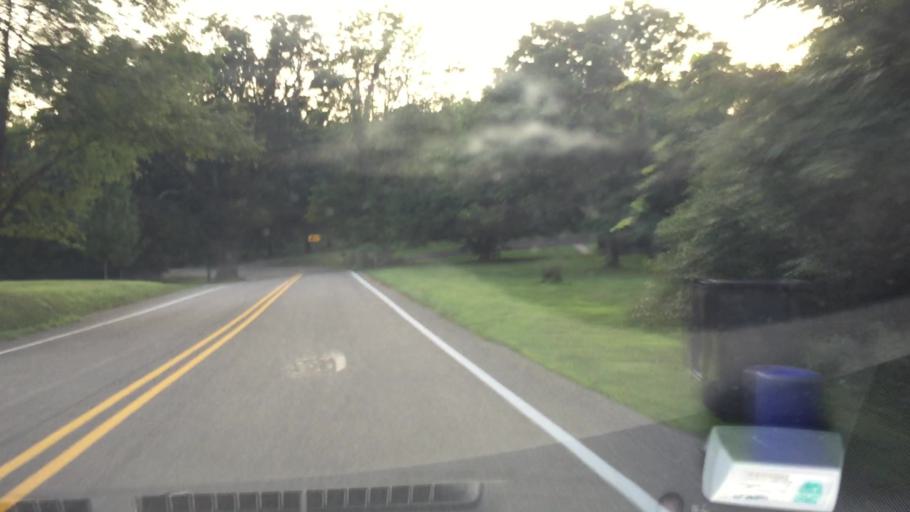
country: US
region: Pennsylvania
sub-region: Butler County
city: Evans City
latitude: 40.7534
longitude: -80.0714
